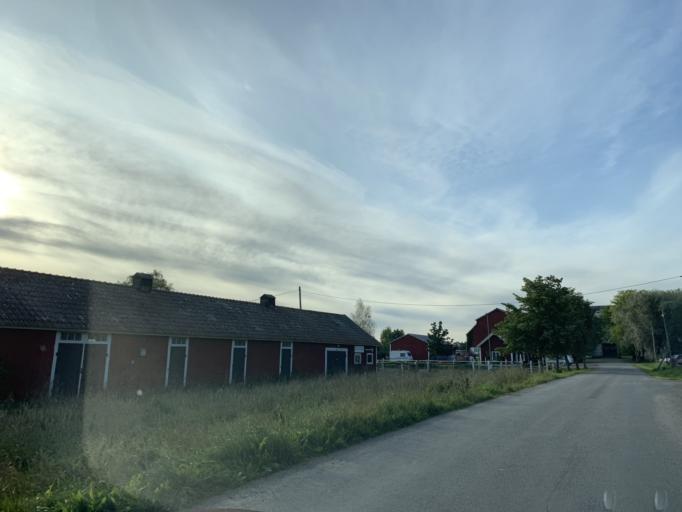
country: SE
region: Stockholm
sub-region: Nynashamns Kommun
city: Osmo
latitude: 59.0411
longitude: 18.0159
